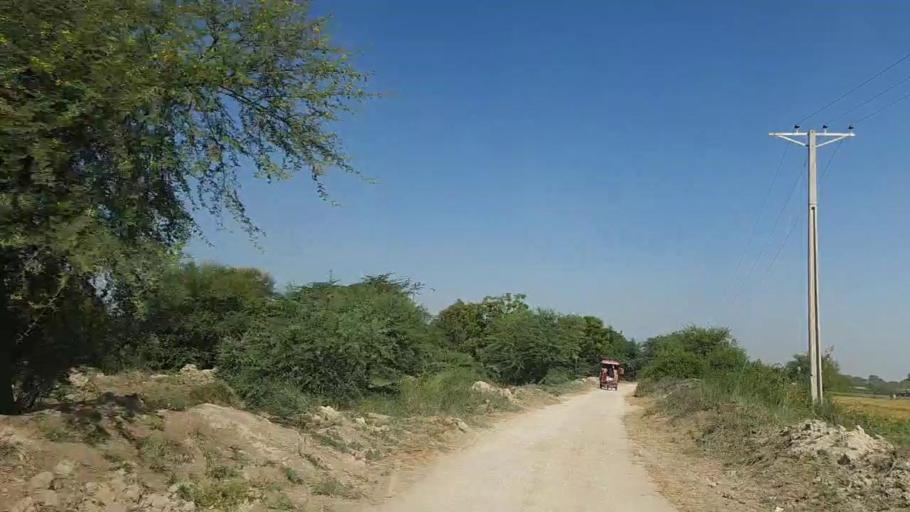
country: PK
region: Sindh
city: Daro Mehar
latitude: 24.7730
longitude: 68.1557
